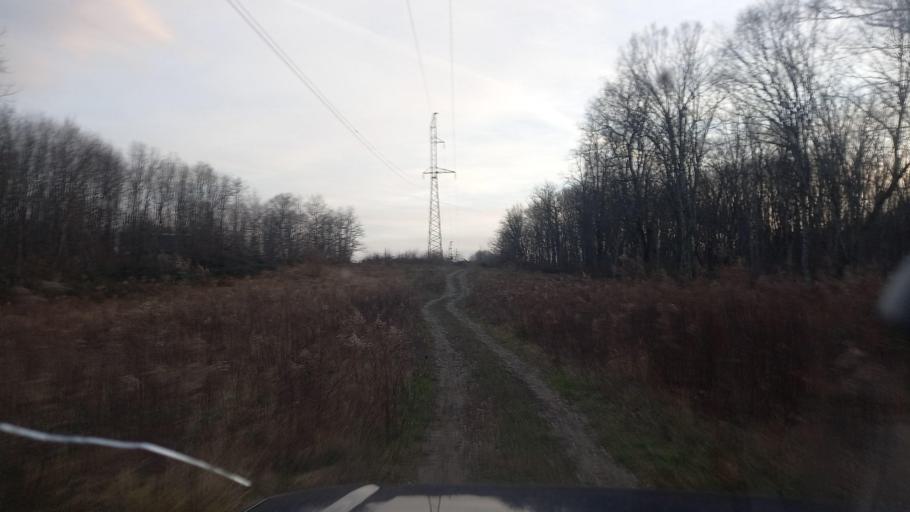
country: RU
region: Krasnodarskiy
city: Goryachiy Klyuch
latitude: 44.3885
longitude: 39.1822
